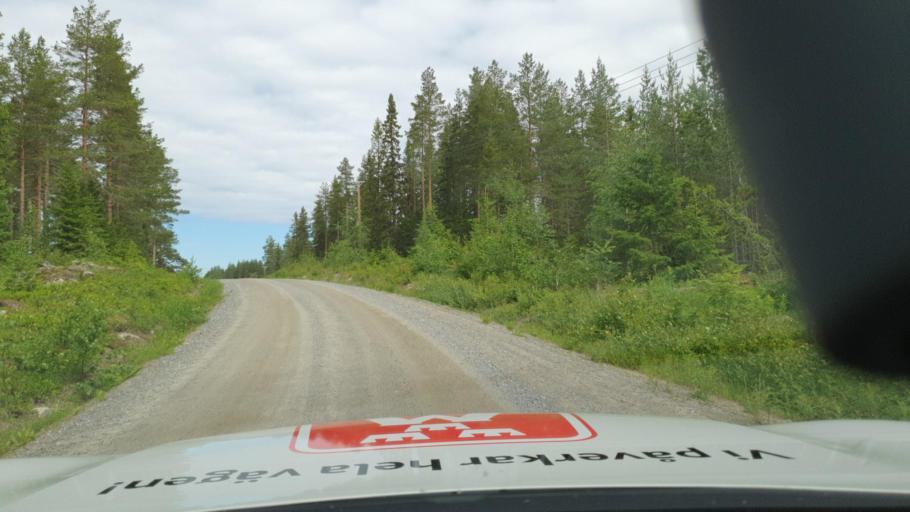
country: SE
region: Vaesterbotten
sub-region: Skelleftea Kommun
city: Langsele
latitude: 64.5713
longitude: 20.3002
